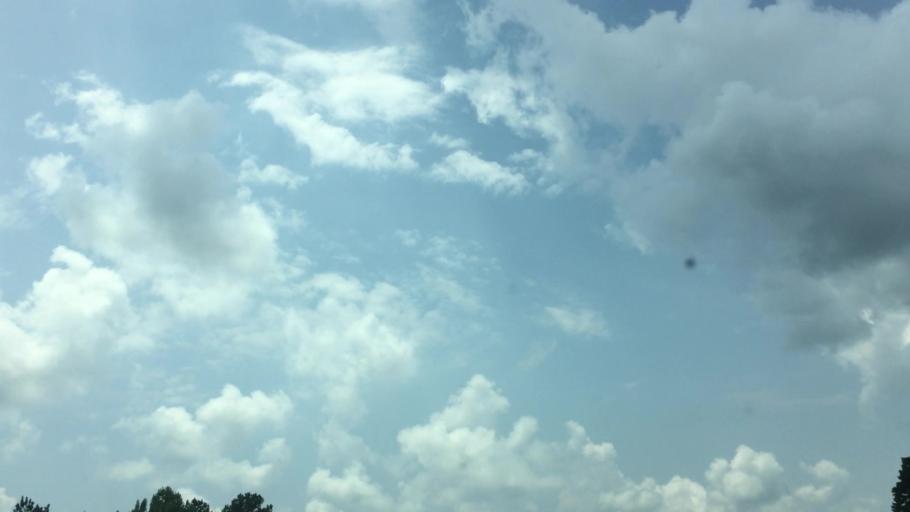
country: US
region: Georgia
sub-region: Fulton County
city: Palmetto
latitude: 33.5744
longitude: -84.6753
